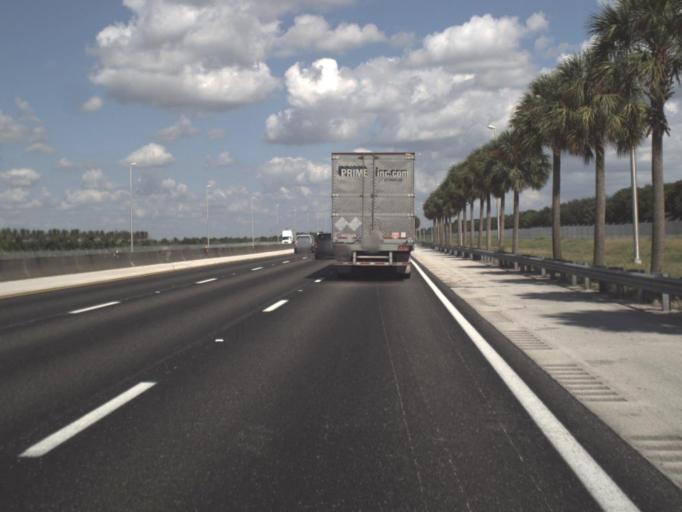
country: US
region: Florida
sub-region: Palm Beach County
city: Villages of Oriole
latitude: 26.4915
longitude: -80.1724
